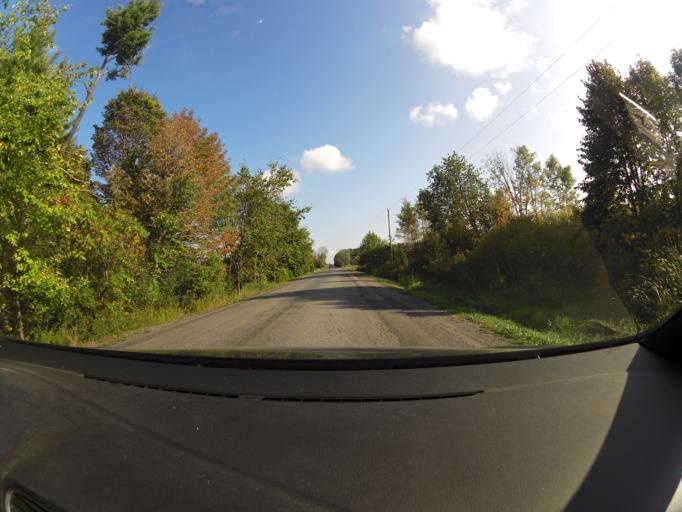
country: CA
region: Ontario
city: Arnprior
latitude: 45.4233
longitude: -76.2298
